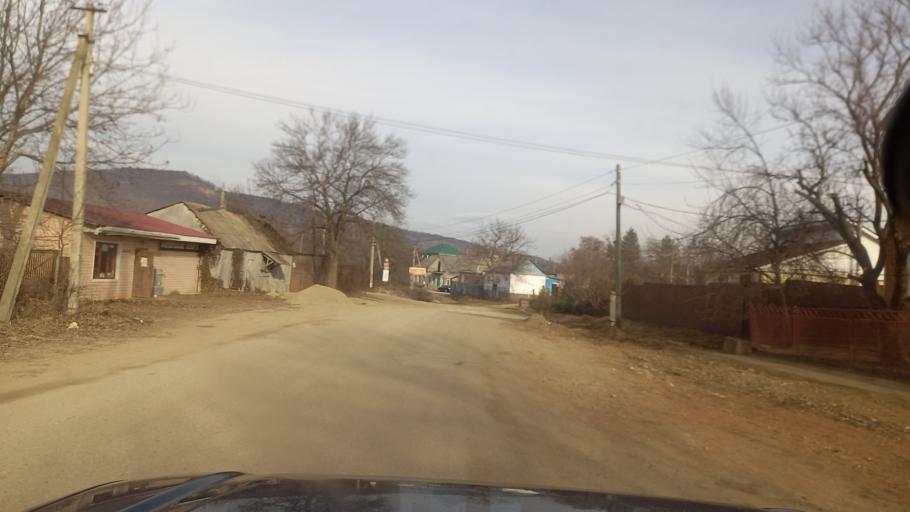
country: RU
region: Adygeya
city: Kamennomostskiy
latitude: 44.2950
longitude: 40.1816
